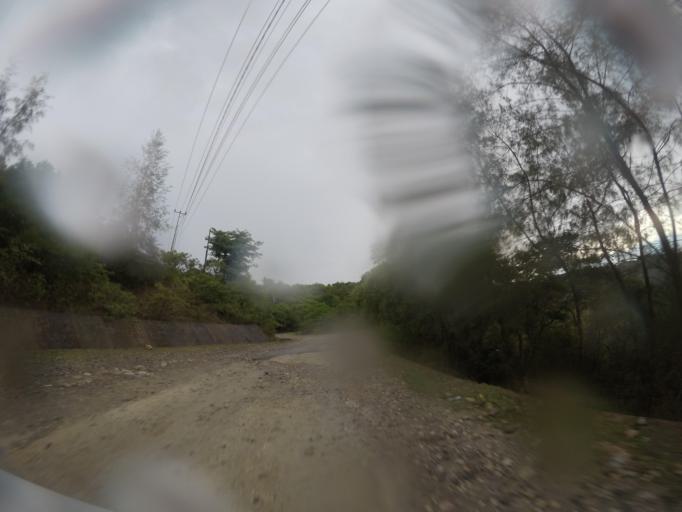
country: TL
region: Bobonaro
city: Maliana
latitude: -8.9632
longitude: 125.0268
